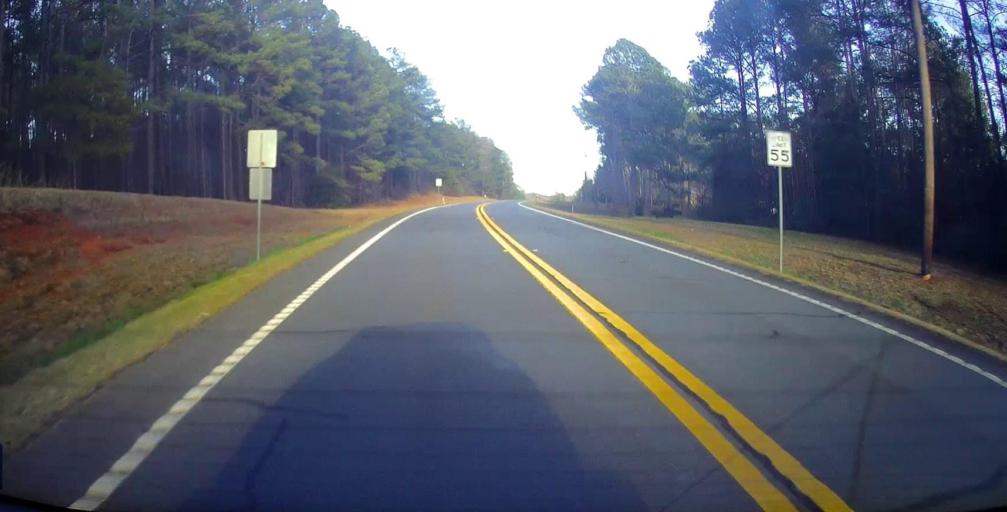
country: US
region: Georgia
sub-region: Talbot County
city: Sardis
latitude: 32.7908
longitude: -84.5532
